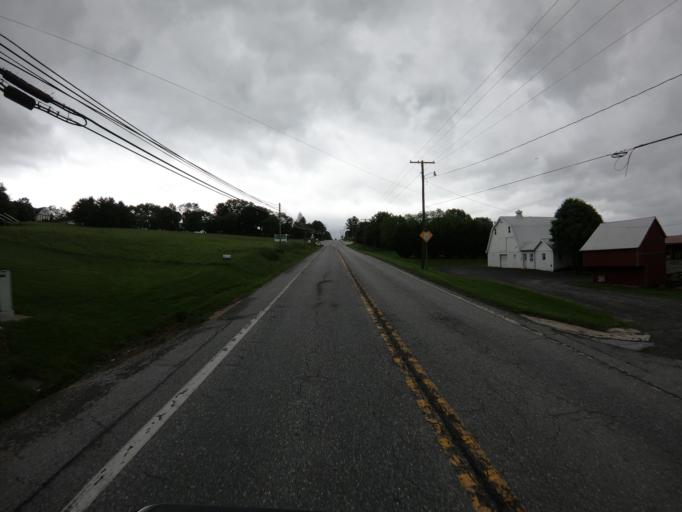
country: US
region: Maryland
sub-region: Frederick County
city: Middletown
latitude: 39.4498
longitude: -77.5616
